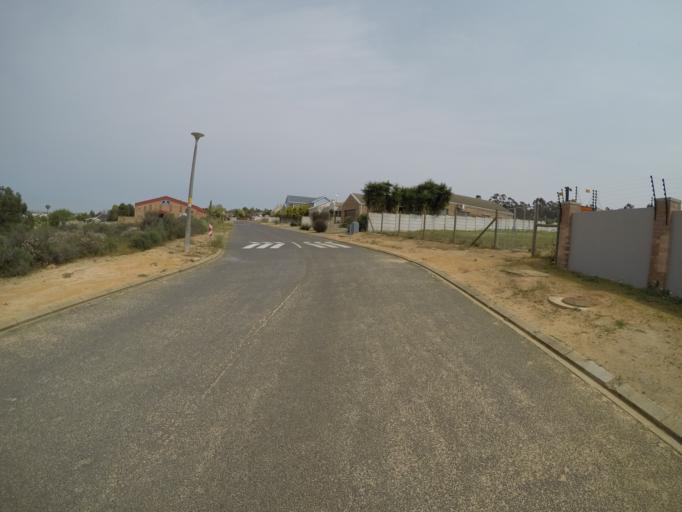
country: ZA
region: Western Cape
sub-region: West Coast District Municipality
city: Malmesbury
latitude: -33.4596
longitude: 18.7423
